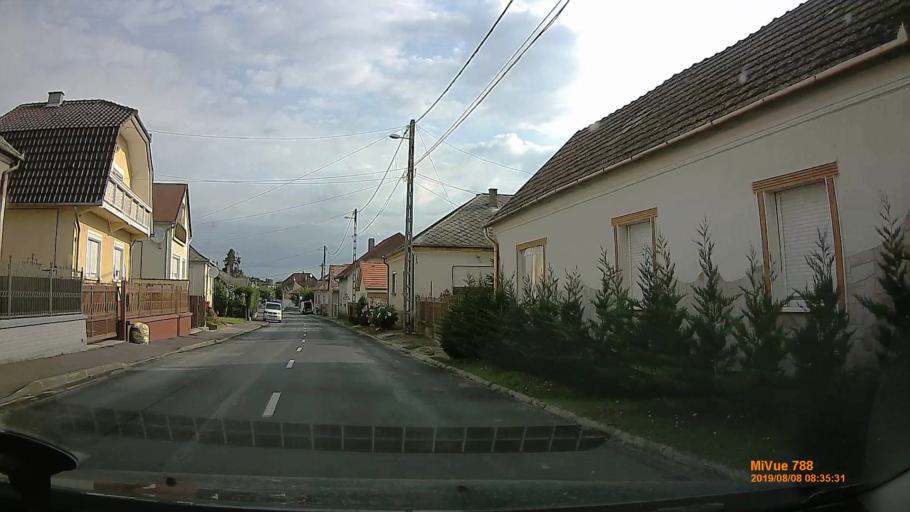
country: HU
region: Zala
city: Nagykanizsa
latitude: 46.4544
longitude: 16.9568
